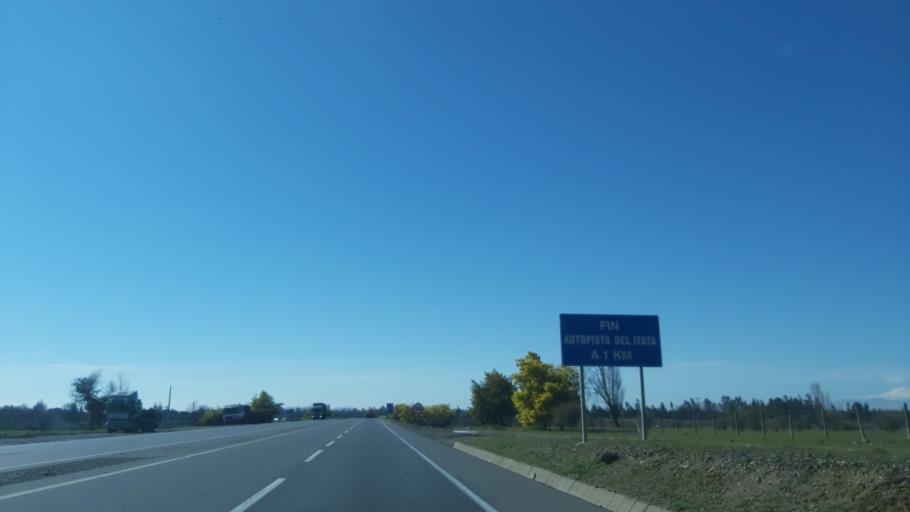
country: CL
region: Biobio
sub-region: Provincia de Nuble
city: Bulnes
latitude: -36.6558
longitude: -72.2438
